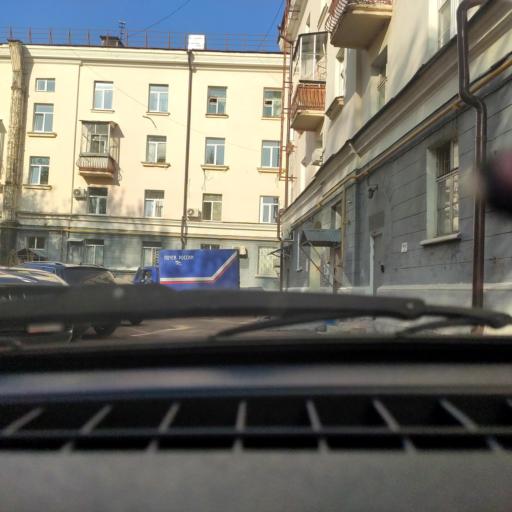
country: RU
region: Bashkortostan
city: Ufa
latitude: 54.7391
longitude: 55.9466
